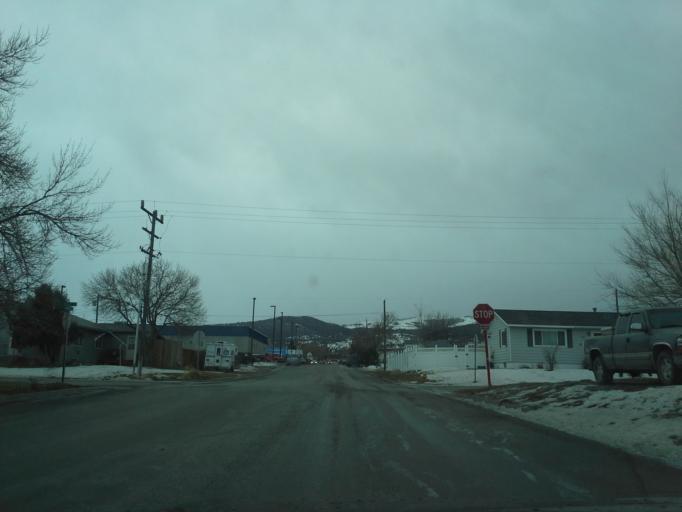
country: US
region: Montana
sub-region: Lewis and Clark County
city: Helena
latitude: 46.6091
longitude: -112.0151
